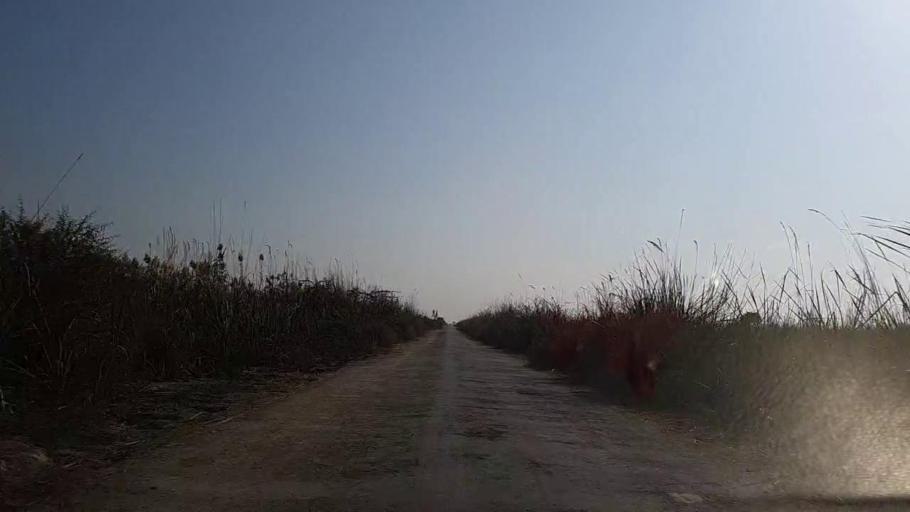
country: PK
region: Sindh
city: Tando Mittha Khan
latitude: 25.8940
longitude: 69.0770
